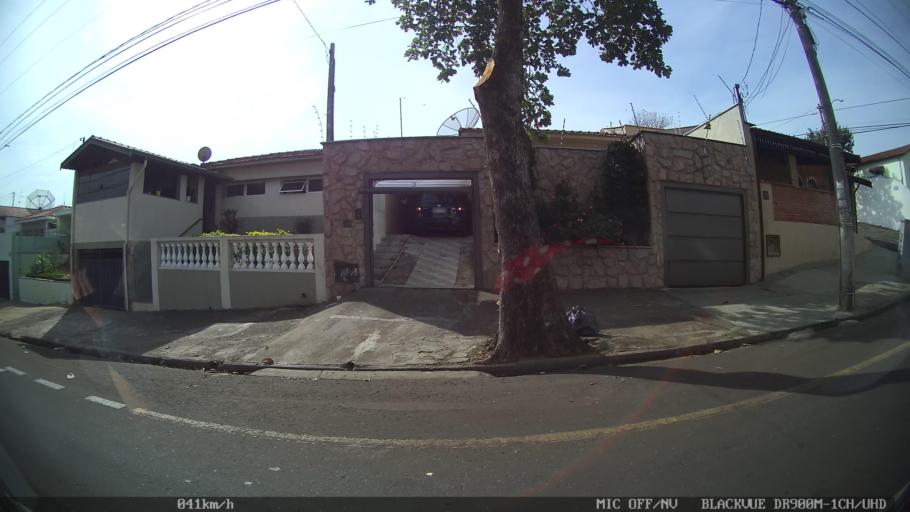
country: BR
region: Sao Paulo
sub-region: Piracicaba
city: Piracicaba
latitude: -22.7329
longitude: -47.6671
